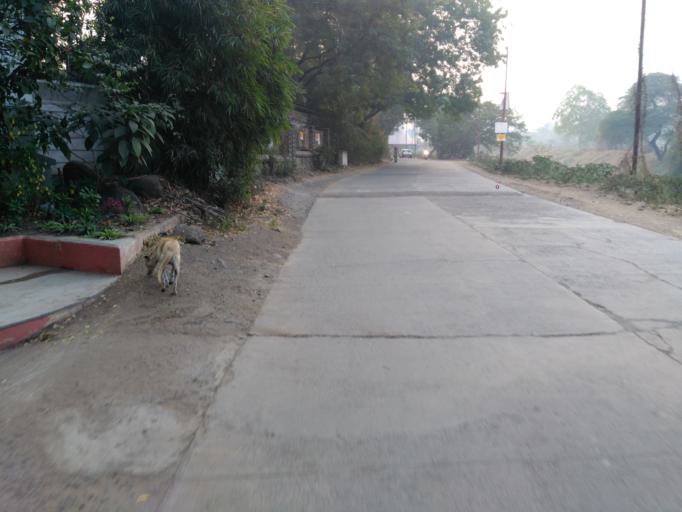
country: IN
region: Maharashtra
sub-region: Pune Division
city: Pune
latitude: 18.4610
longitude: 73.9073
